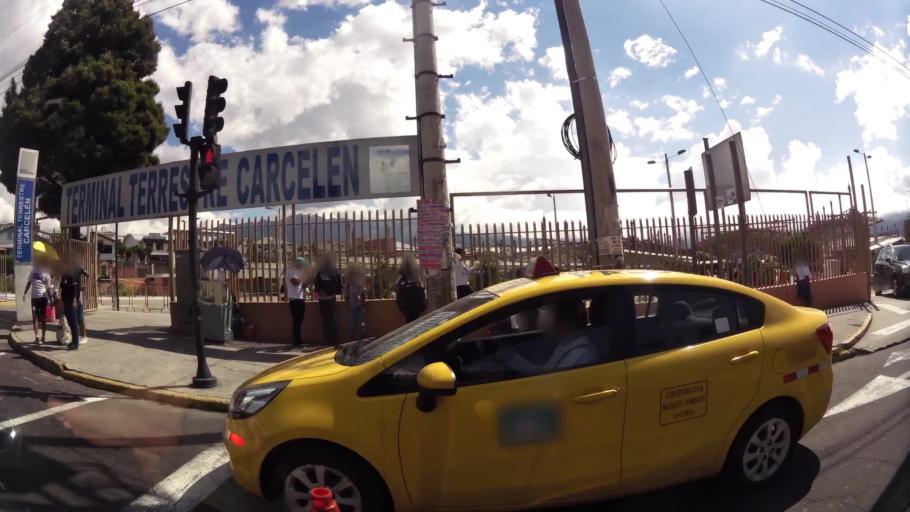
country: EC
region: Pichincha
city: Quito
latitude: -0.1008
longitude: -78.4693
